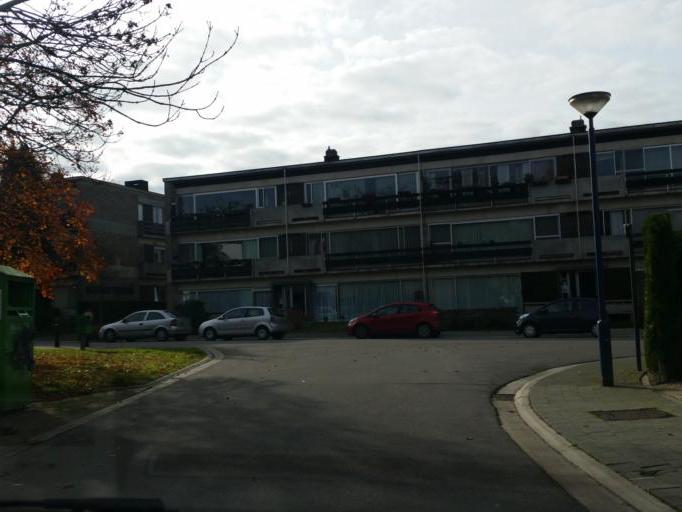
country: BE
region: Flanders
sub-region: Provincie Antwerpen
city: Kontich
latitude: 51.1418
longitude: 4.4514
